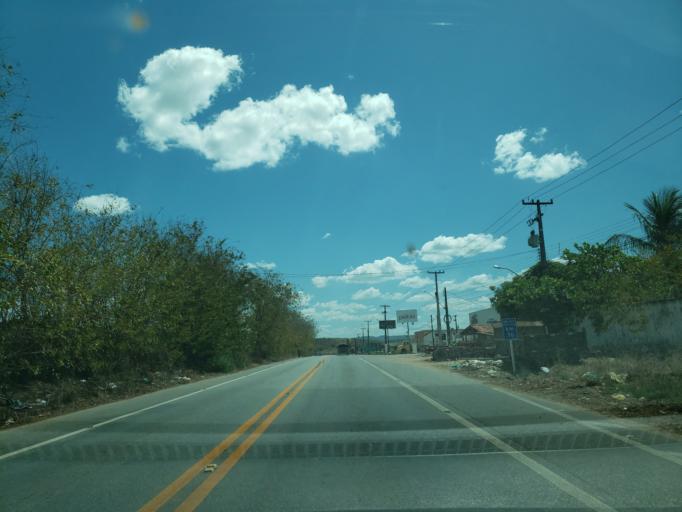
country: BR
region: Alagoas
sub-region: Uniao Dos Palmares
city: Uniao dos Palmares
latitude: -9.1677
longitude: -36.0223
